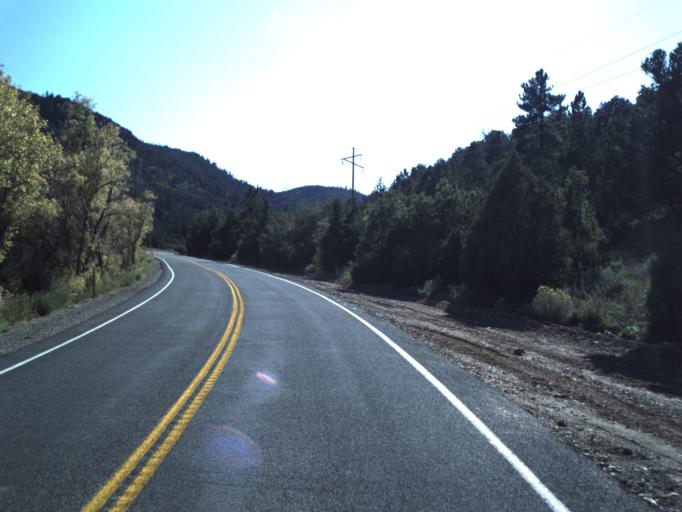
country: US
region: Utah
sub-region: Iron County
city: Parowan
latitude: 37.7756
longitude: -112.8384
